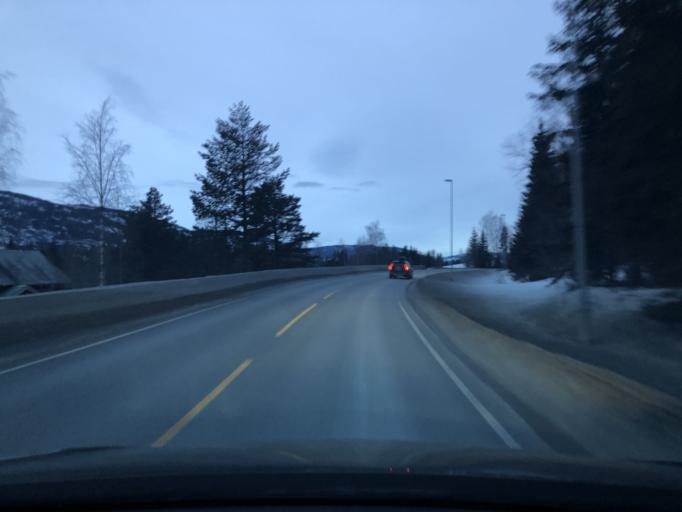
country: NO
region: Oppland
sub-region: Sor-Aurdal
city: Bagn
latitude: 60.8985
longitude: 9.4551
